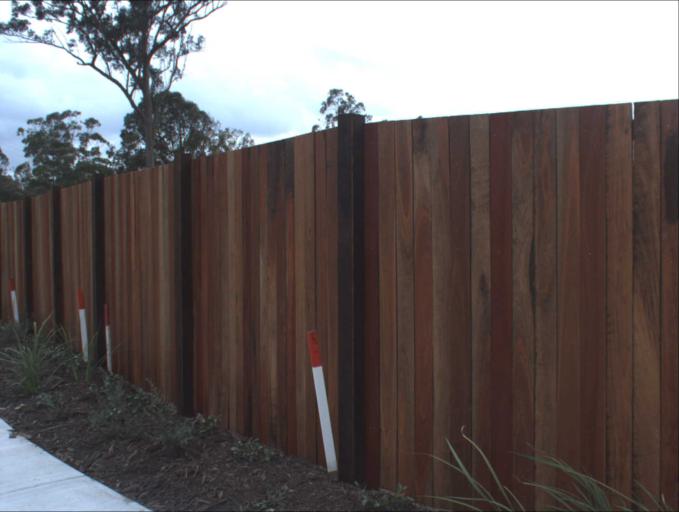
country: AU
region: Queensland
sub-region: Logan
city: Logan Reserve
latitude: -27.7127
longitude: 153.1076
